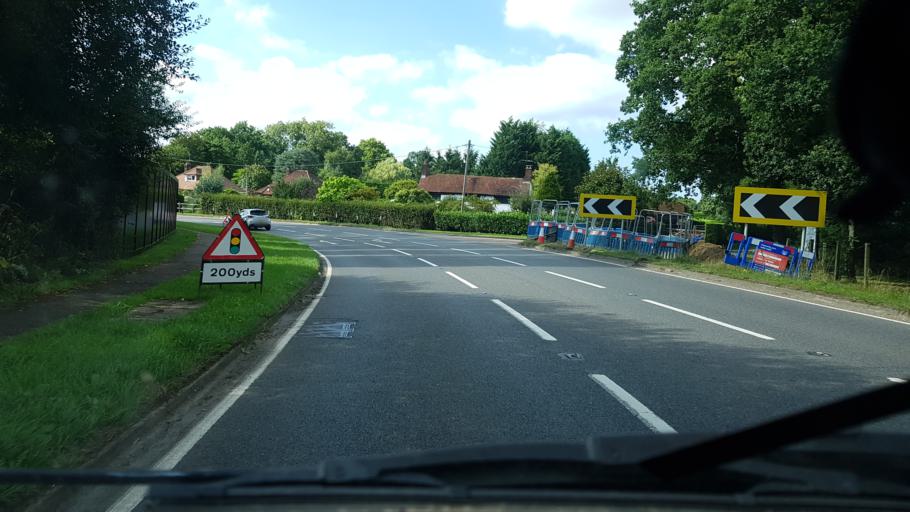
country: GB
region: England
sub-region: Surrey
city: Cranleigh
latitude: 51.1060
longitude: -0.5106
